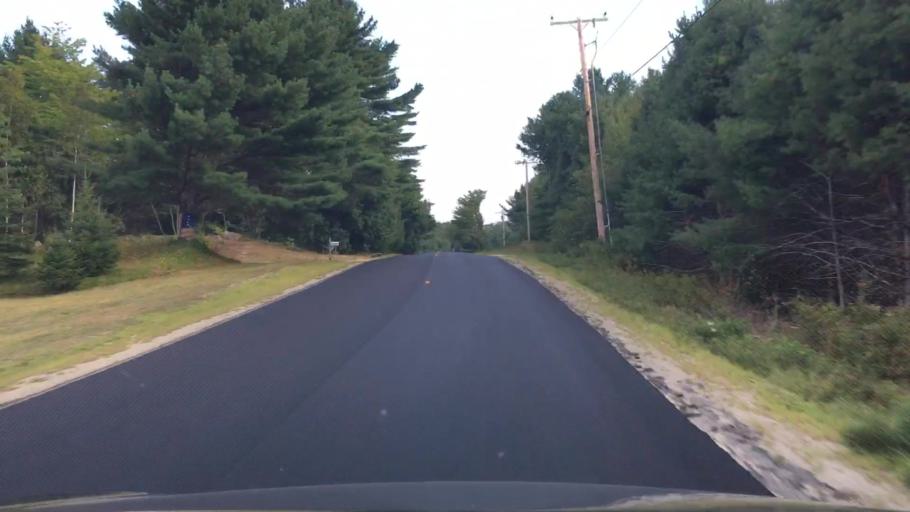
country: US
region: Maine
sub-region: Hancock County
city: Surry
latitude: 44.5292
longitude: -68.6119
